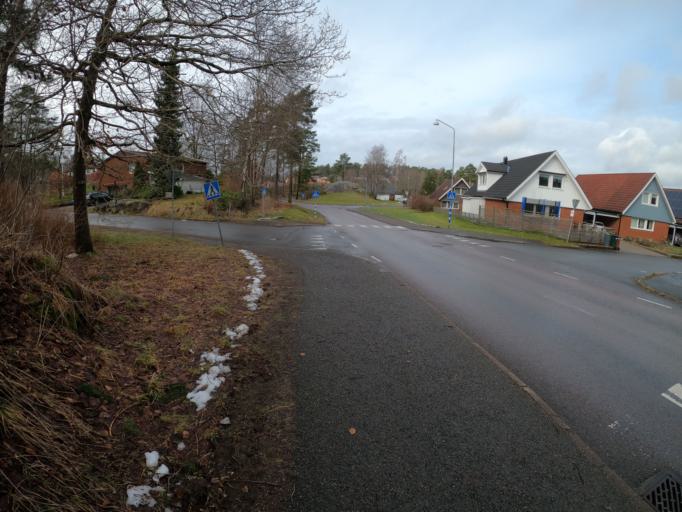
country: SE
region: Vaestra Goetaland
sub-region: Harryda Kommun
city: Molnlycke
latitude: 57.6485
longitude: 12.1191
